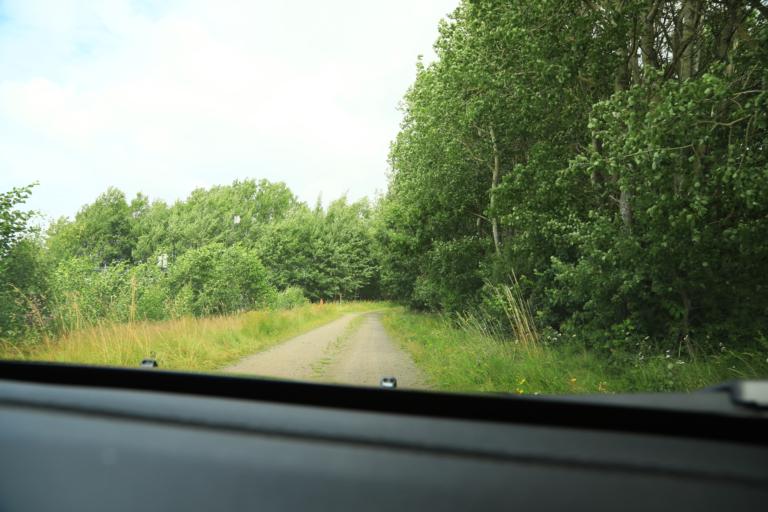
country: SE
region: Halland
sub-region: Varbergs Kommun
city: Traslovslage
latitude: 57.1217
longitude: 12.3155
